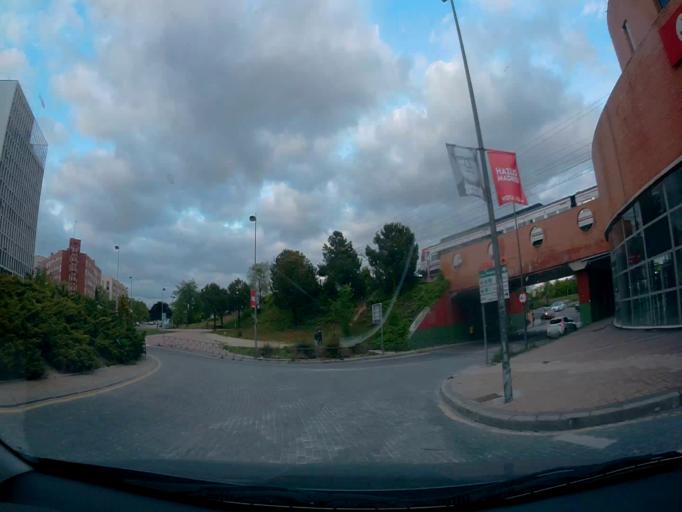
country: ES
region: Madrid
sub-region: Provincia de Madrid
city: Alcorcon
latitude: 40.3422
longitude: -3.8426
